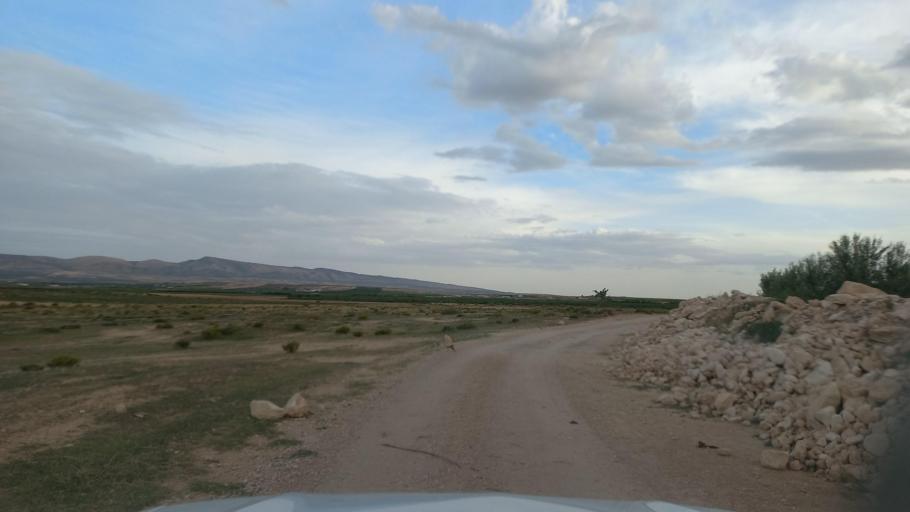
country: TN
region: Al Qasrayn
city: Sbiba
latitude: 35.4312
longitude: 9.0985
